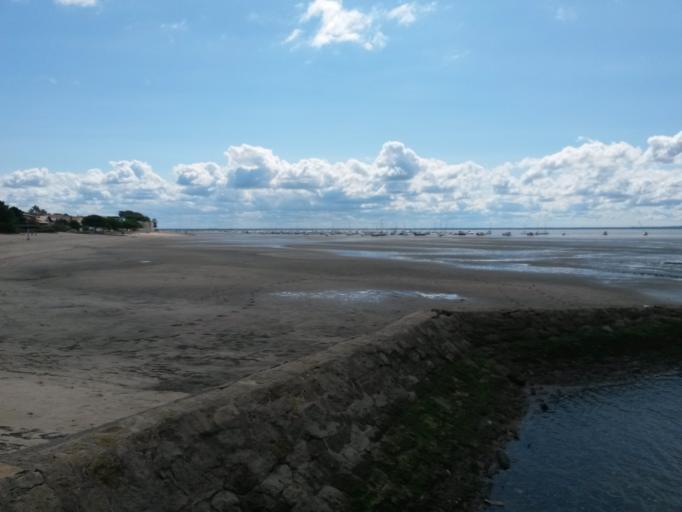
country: FR
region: Aquitaine
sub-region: Departement de la Gironde
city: Andernos-les-Bains
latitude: 44.7341
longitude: -1.0932
